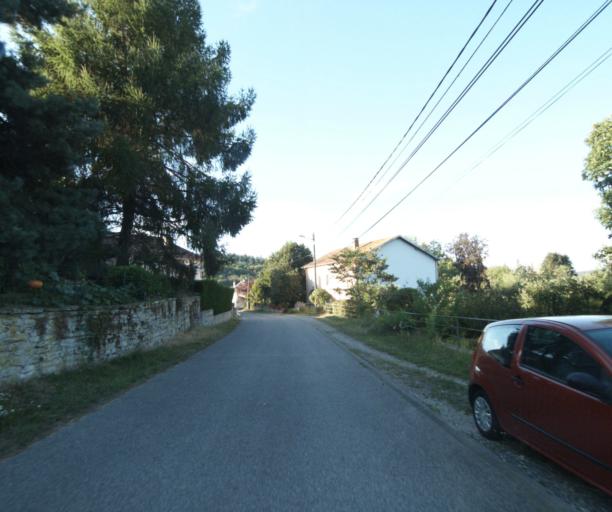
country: FR
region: Lorraine
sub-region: Departement des Vosges
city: Chantraine
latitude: 48.1324
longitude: 6.4424
